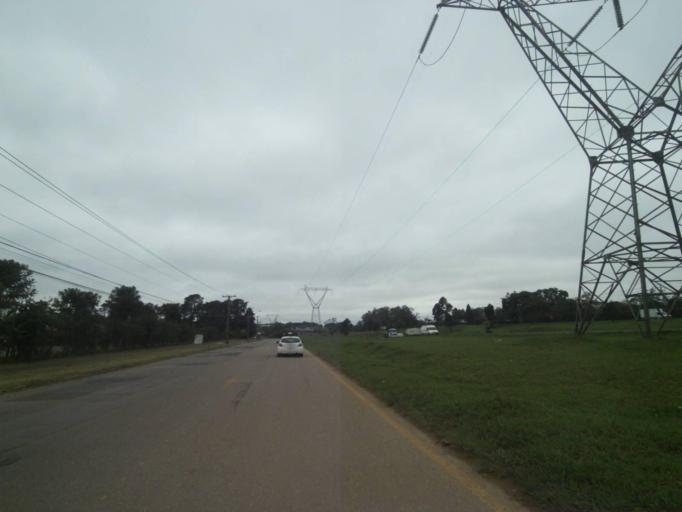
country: BR
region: Parana
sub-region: Araucaria
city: Araucaria
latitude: -25.5473
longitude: -49.3213
